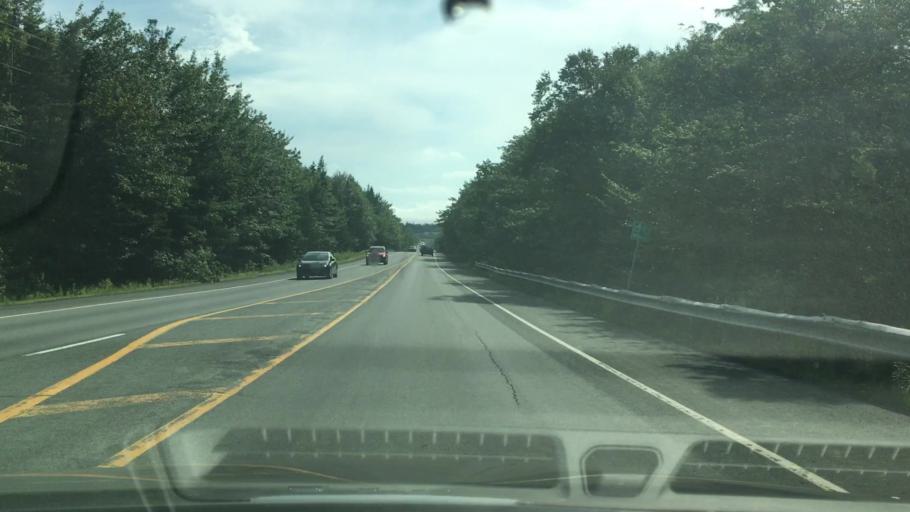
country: CA
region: Nova Scotia
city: Dartmouth
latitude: 44.7095
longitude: -63.8443
